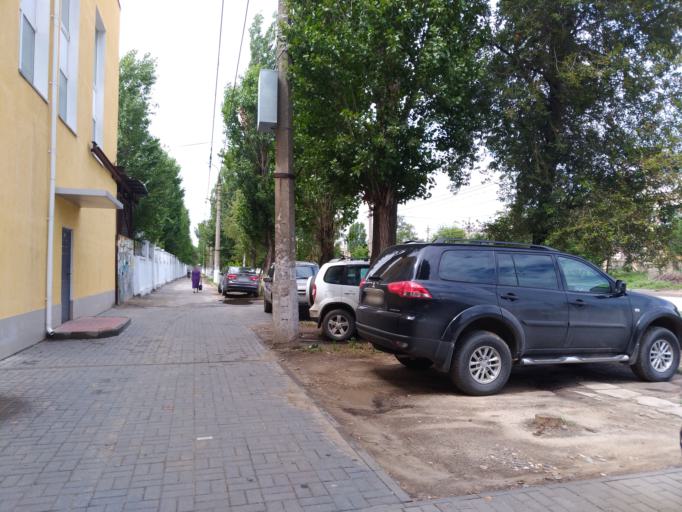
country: RU
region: Volgograd
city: Volgograd
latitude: 48.7164
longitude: 44.4864
